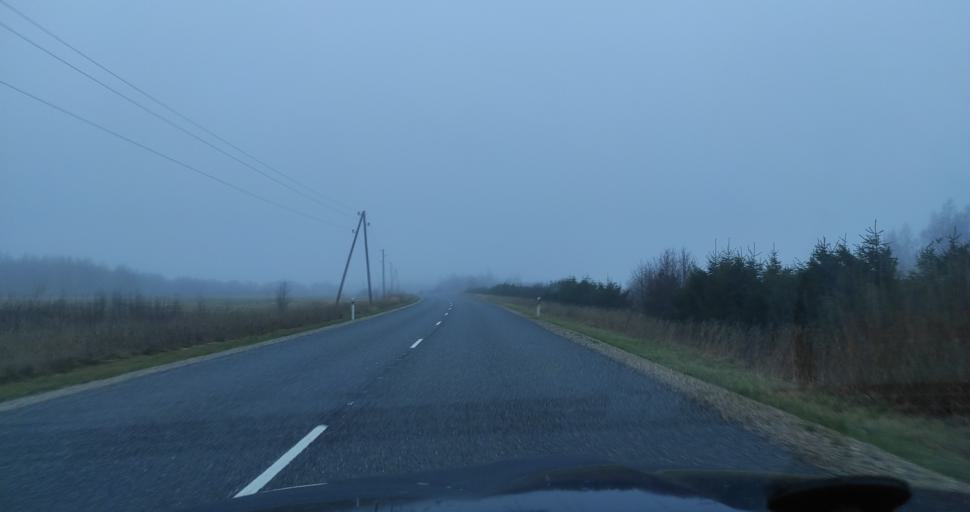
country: LV
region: Alsunga
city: Alsunga
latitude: 56.9919
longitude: 21.3659
